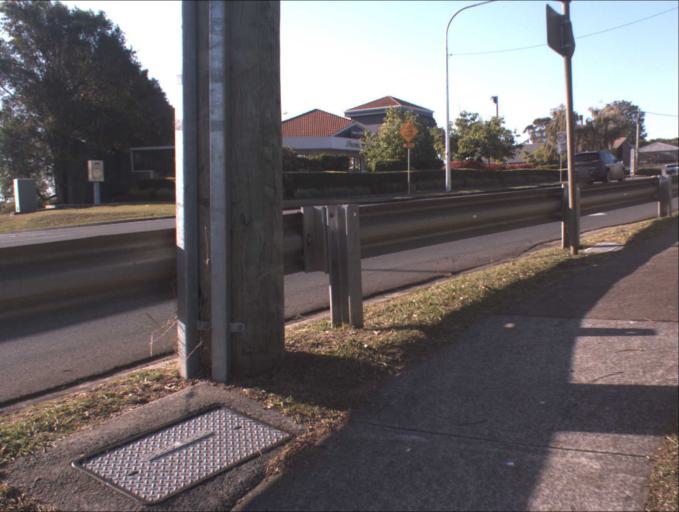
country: AU
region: Queensland
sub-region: Logan
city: Springwood
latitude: -27.6067
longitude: 153.1201
